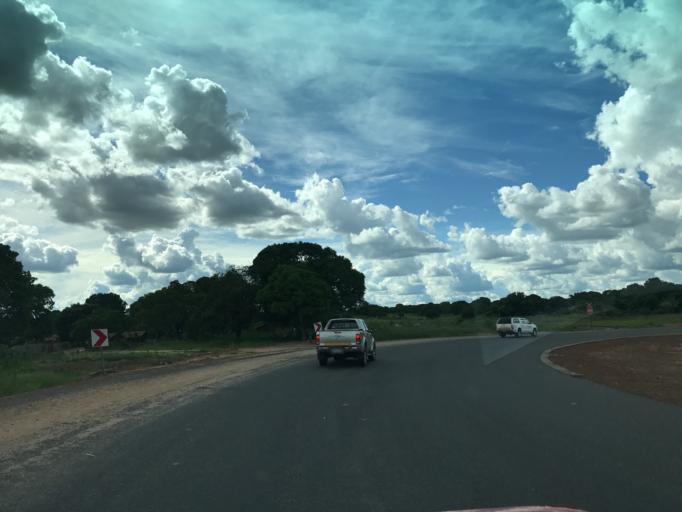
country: MZ
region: Nampula
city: Nampula
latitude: -15.0136
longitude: 39.1231
